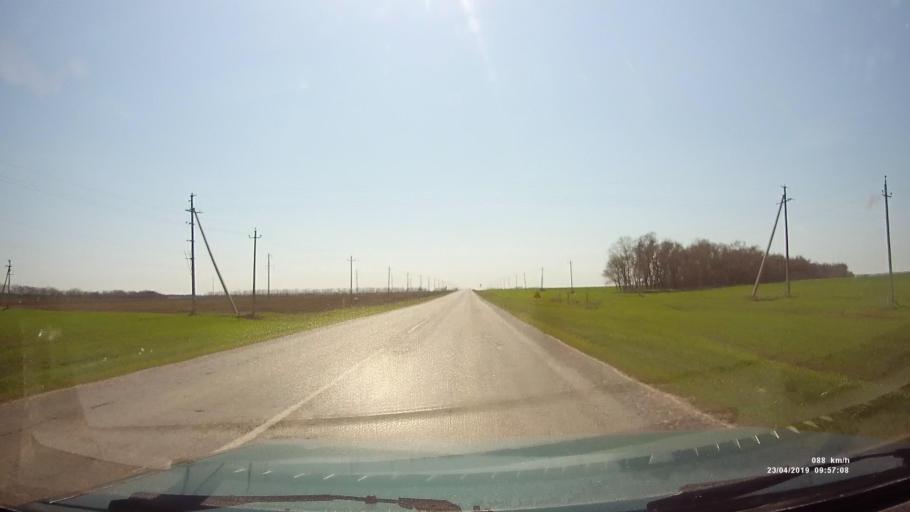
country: RU
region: Rostov
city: Orlovskiy
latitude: 46.7918
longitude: 42.0812
